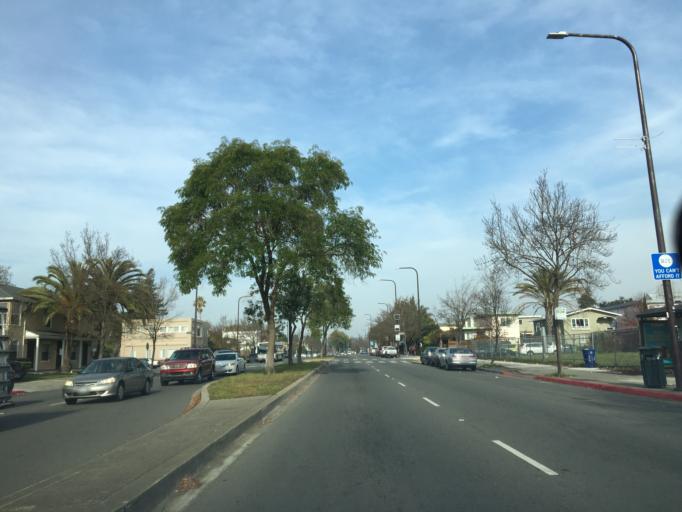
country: US
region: California
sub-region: Alameda County
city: Emeryville
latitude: 37.8481
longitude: -122.2778
